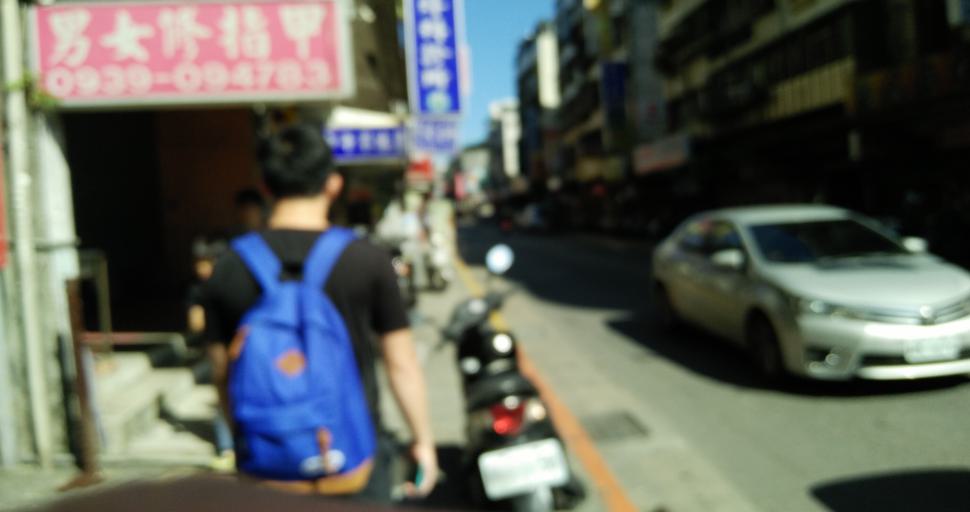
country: TW
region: Taipei
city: Taipei
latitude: 25.0686
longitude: 121.6184
